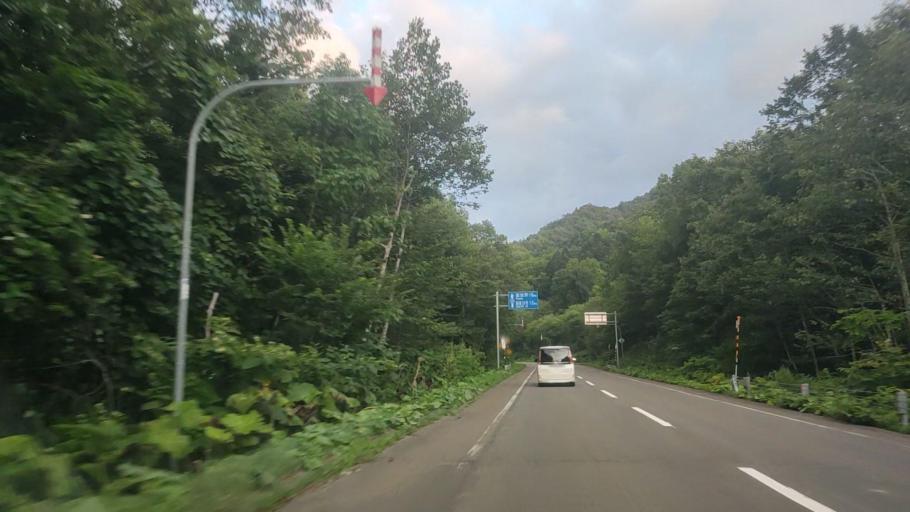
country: JP
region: Hokkaido
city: Ashibetsu
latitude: 43.3673
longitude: 142.2288
